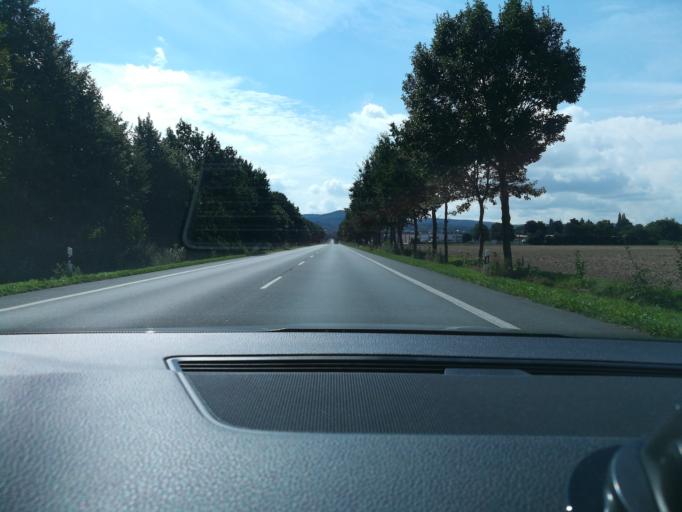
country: DE
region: North Rhine-Westphalia
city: Lubbecke
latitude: 52.3219
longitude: 8.6250
